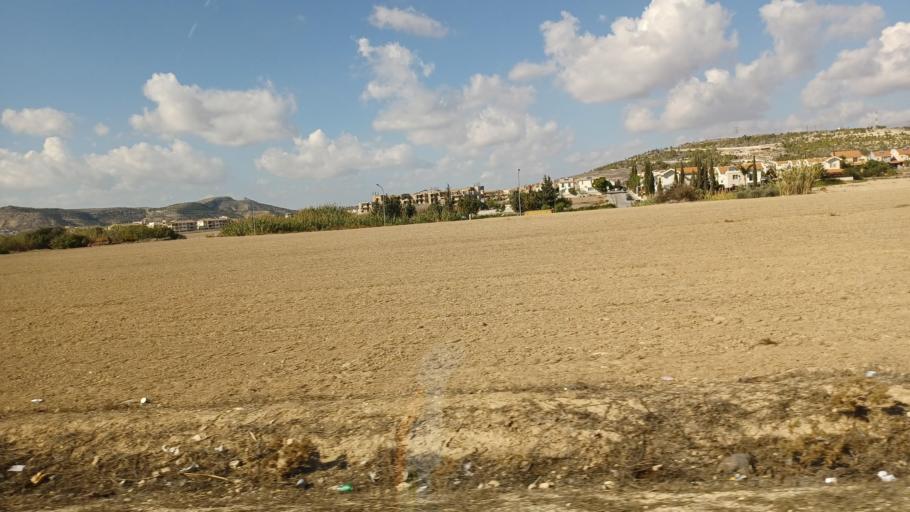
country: CY
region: Larnaka
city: Pyla
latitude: 34.9955
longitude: 33.6844
